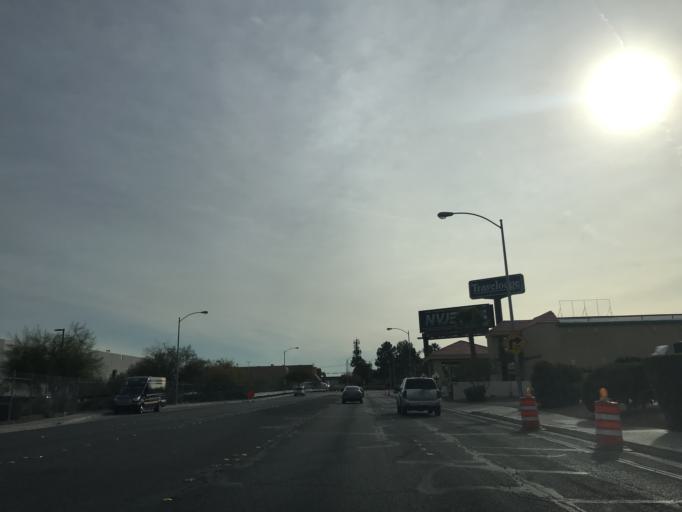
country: US
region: Nevada
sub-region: Clark County
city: Paradise
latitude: 36.0991
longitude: -115.1639
